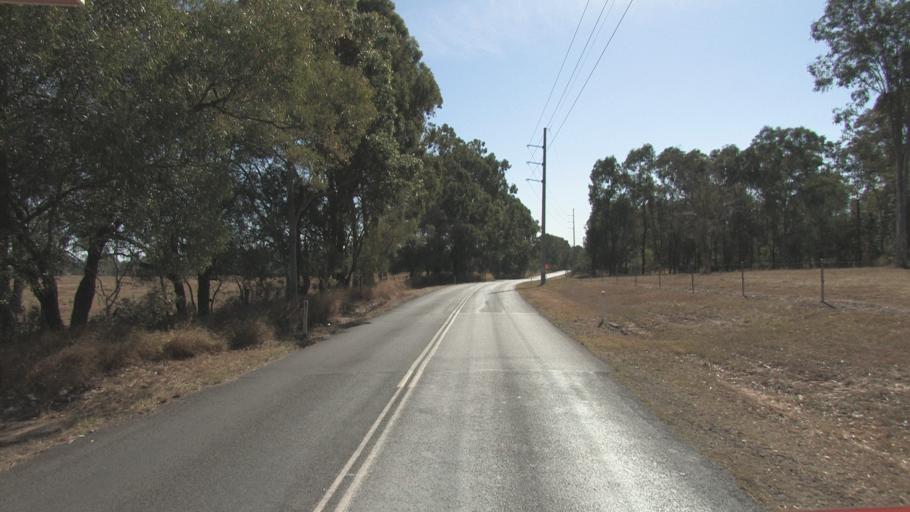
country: AU
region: Queensland
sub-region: Logan
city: Cedar Vale
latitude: -27.8650
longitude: 153.0177
